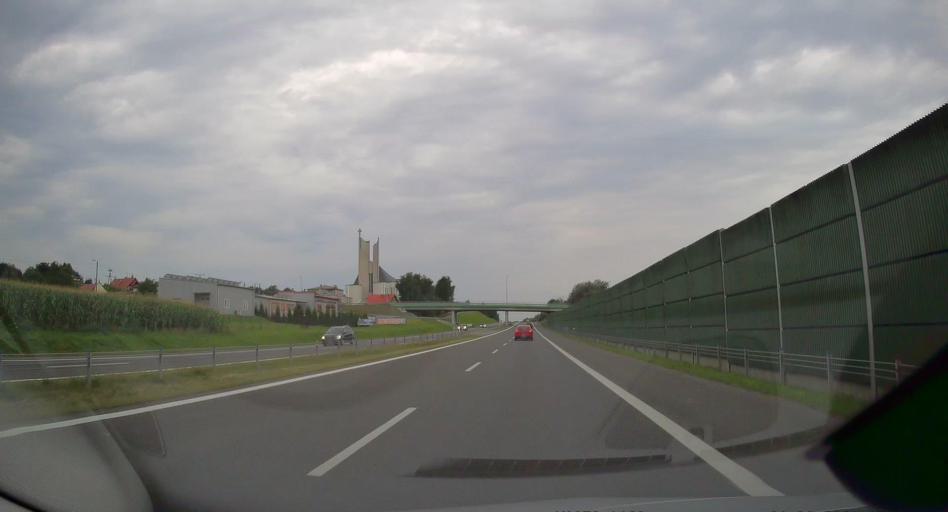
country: PL
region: Lesser Poland Voivodeship
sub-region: Powiat tarnowski
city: Koszyce Wielkie
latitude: 49.9877
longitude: 20.9525
